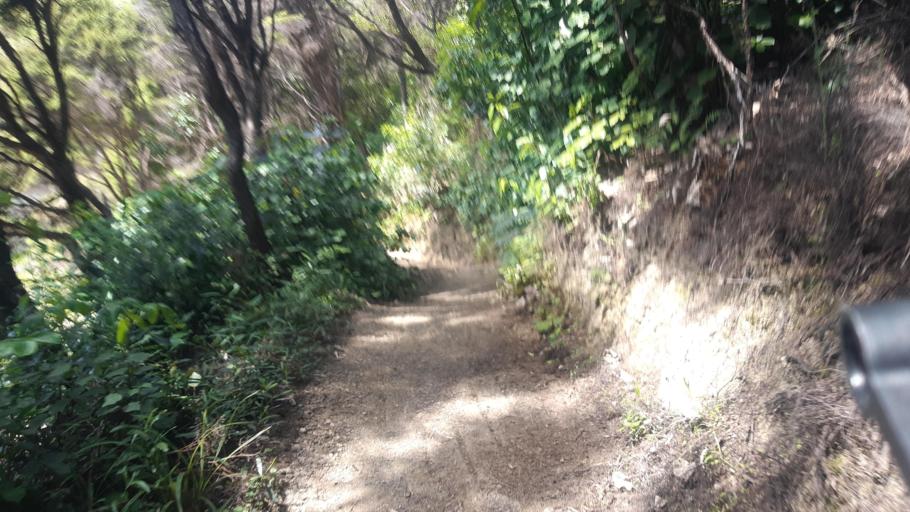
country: NZ
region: Marlborough
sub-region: Marlborough District
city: Picton
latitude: -41.2573
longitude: 174.0361
